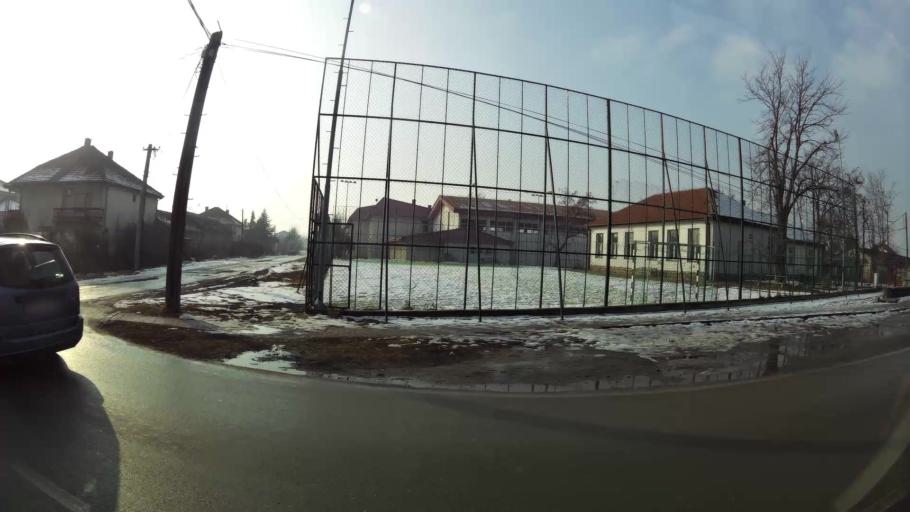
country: MK
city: Kadino
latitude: 41.9693
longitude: 21.5964
